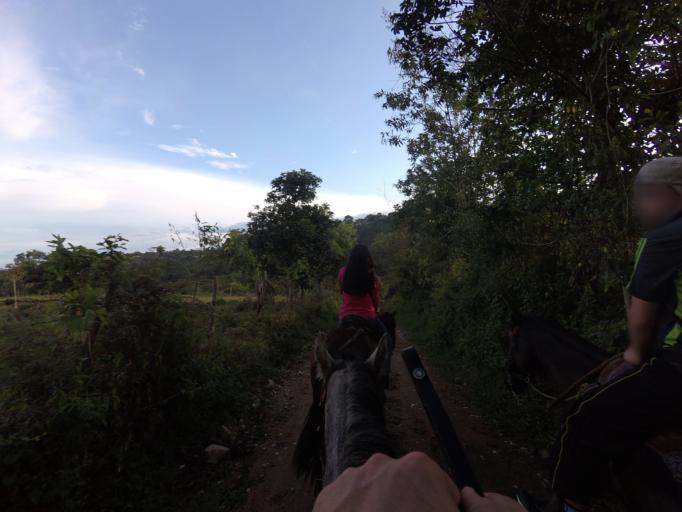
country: CO
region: Huila
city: San Agustin
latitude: 1.9000
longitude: -76.2729
